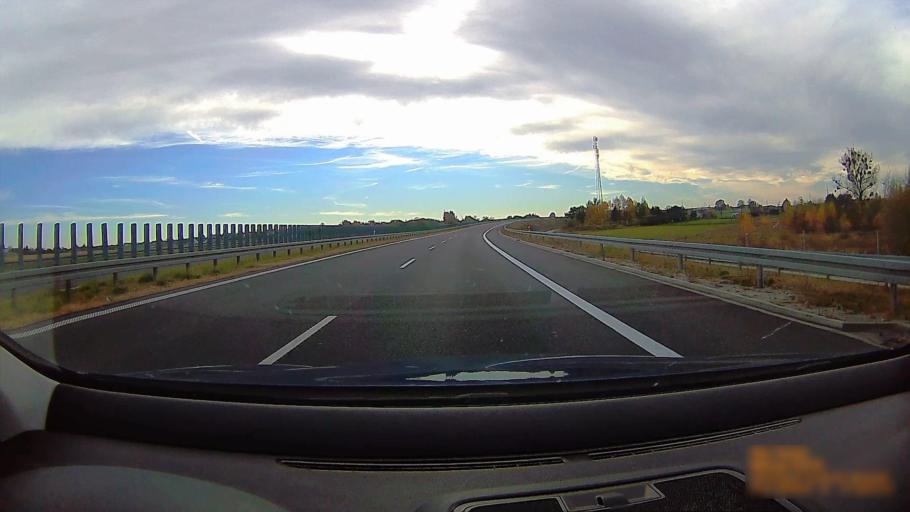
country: PL
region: Greater Poland Voivodeship
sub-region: Powiat ostrowski
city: Ostrow Wielkopolski
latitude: 51.6442
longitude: 17.8751
